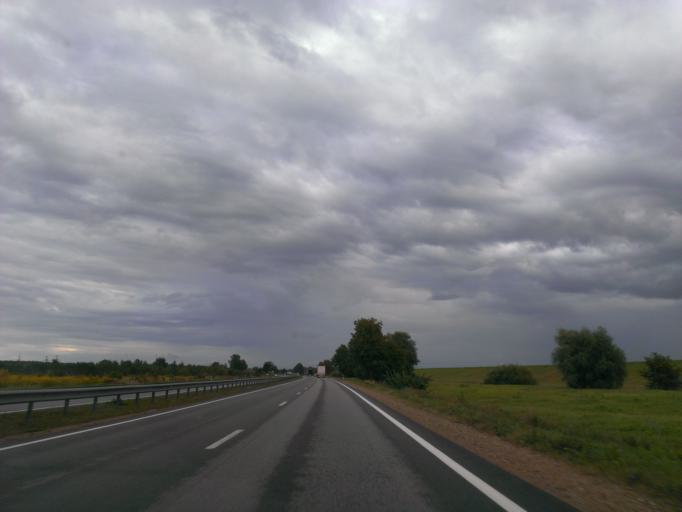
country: LV
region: Salaspils
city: Salaspils
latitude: 56.8481
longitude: 24.3499
